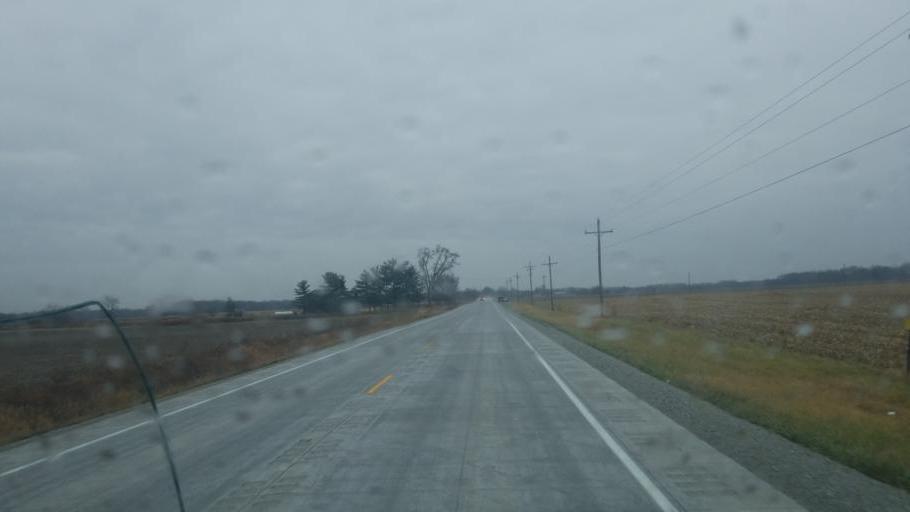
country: US
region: Indiana
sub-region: Shelby County
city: Geneva
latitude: 39.4117
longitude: -85.7508
